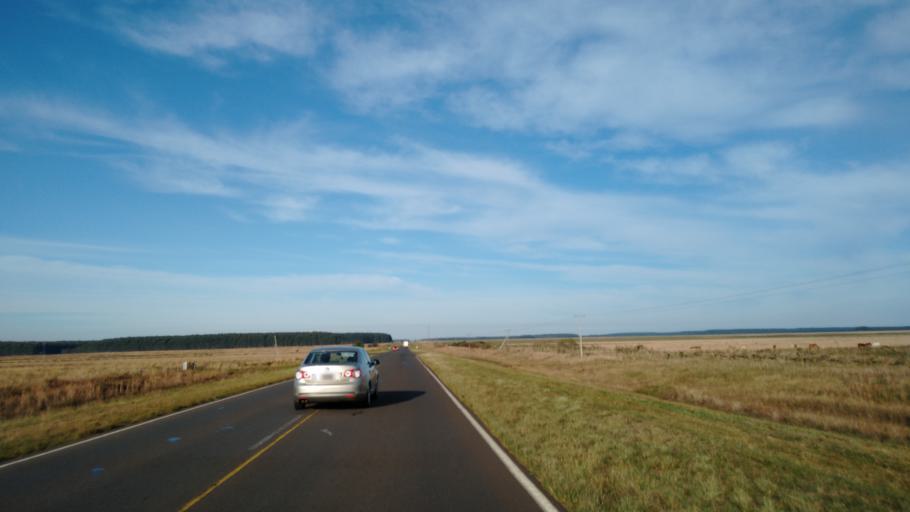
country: AR
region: Corrientes
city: La Cruz
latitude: -29.2973
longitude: -56.7717
